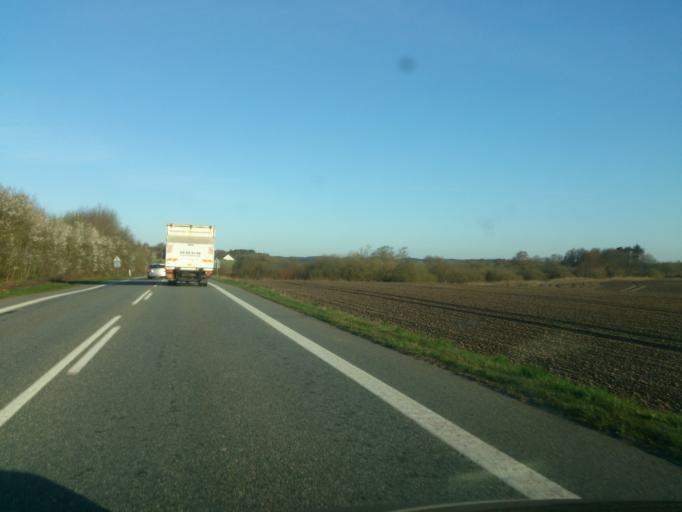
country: DK
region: Central Jutland
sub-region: Favrskov Kommune
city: Ulstrup
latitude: 56.4471
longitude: 9.7374
